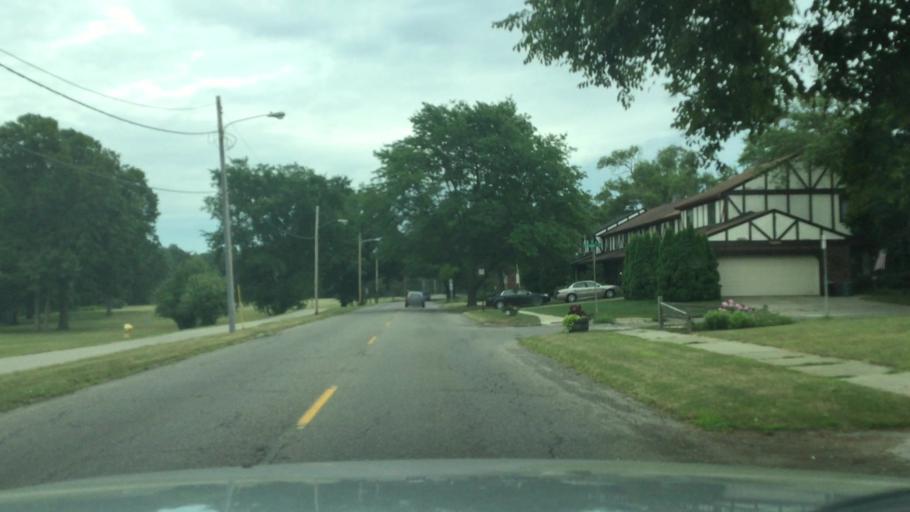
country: US
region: Michigan
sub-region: Genesee County
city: Flint
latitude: 43.0132
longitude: -83.7263
